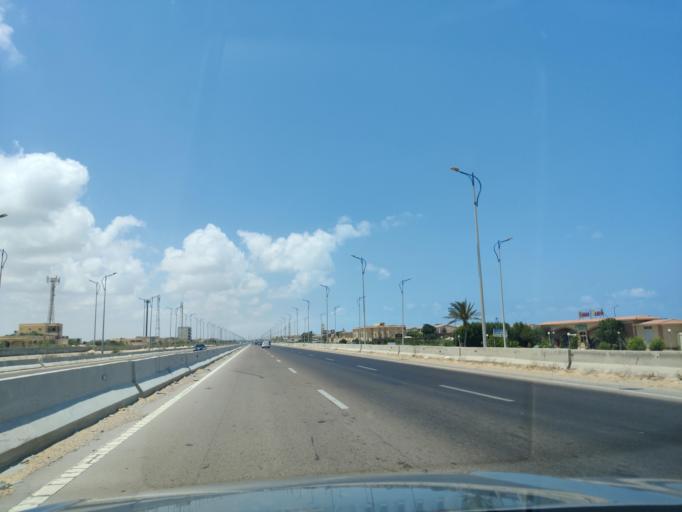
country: EG
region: Muhafazat Matruh
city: Al `Alamayn
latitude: 30.9064
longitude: 29.4284
